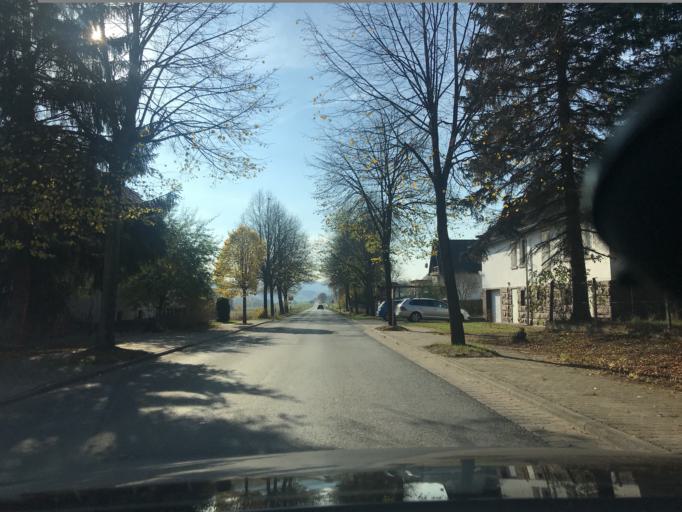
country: DE
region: Hesse
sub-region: Regierungsbezirk Kassel
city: Grossalmerode
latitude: 51.2125
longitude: 9.7939
